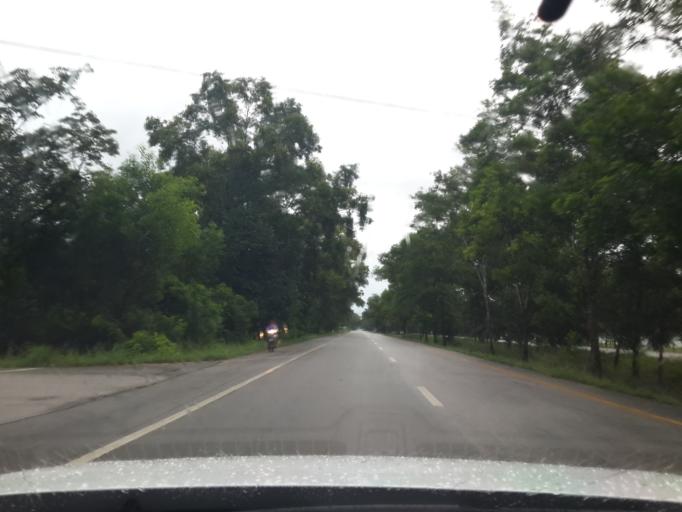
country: TH
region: Songkhla
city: Na Mom
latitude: 6.9858
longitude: 100.6560
